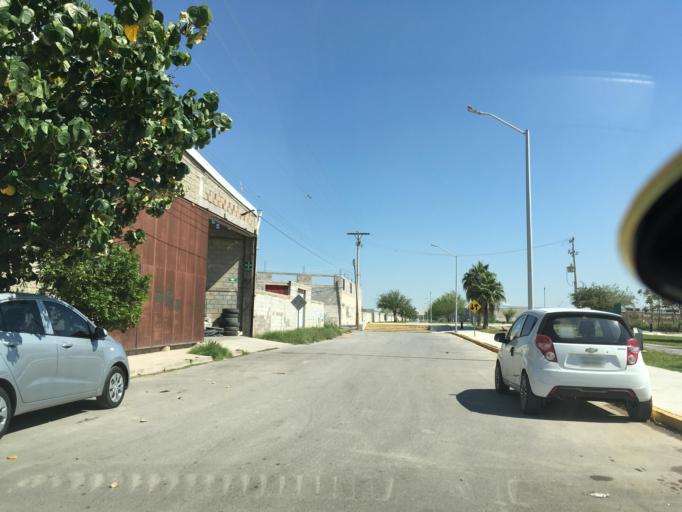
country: MX
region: Coahuila
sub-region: Torreon
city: Fraccionamiento la Noria
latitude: 25.5256
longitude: -103.3767
